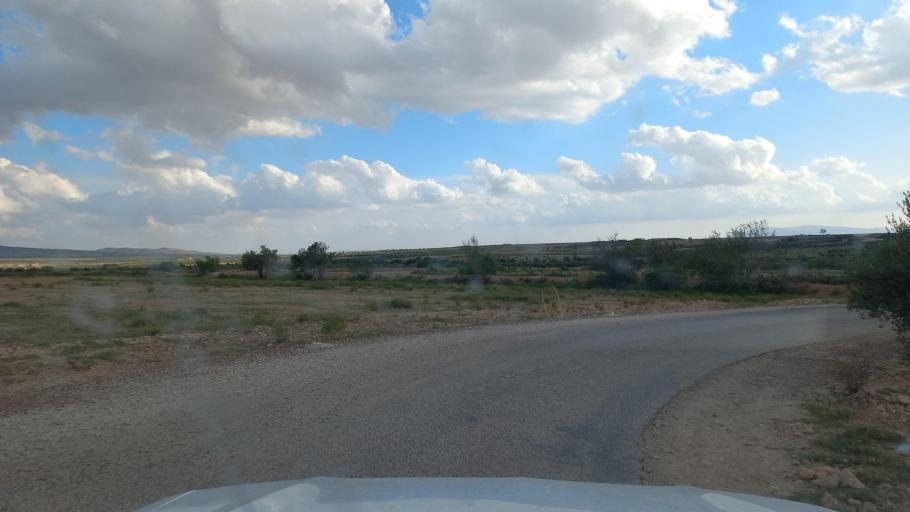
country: TN
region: Al Qasrayn
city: Sbiba
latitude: 35.3763
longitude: 9.0726
